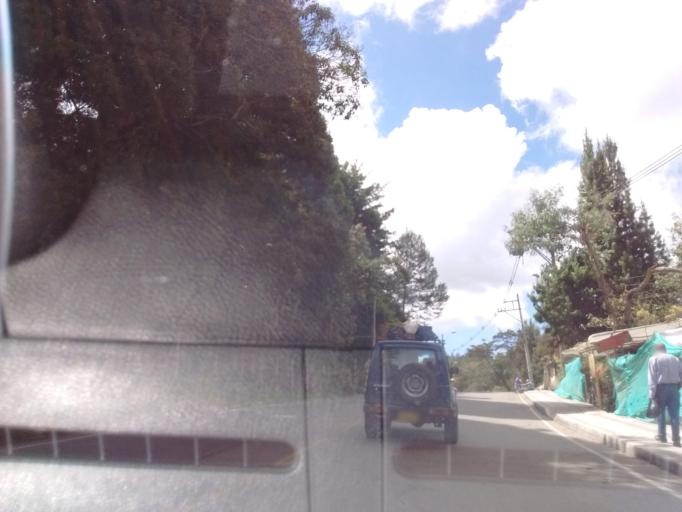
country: CO
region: Antioquia
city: Medellin
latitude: 6.2106
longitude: -75.4992
